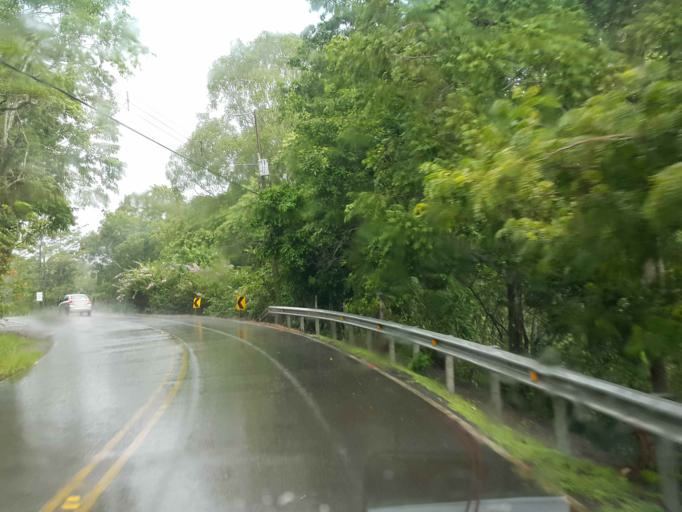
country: CR
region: Guanacaste
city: Juntas
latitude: 10.2126
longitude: -84.8501
